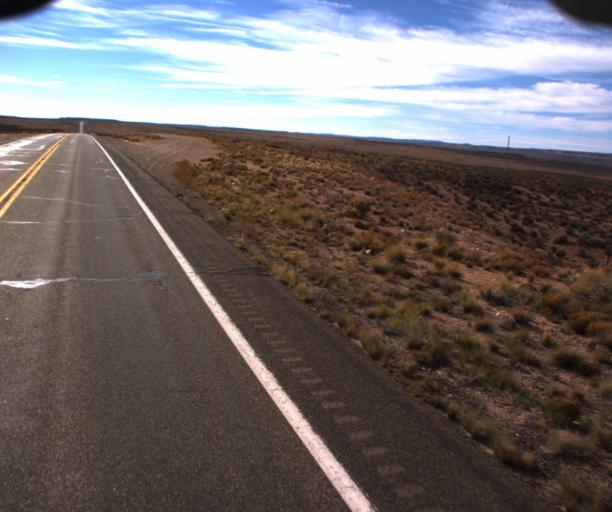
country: US
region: Arizona
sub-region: Coconino County
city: LeChee
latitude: 36.7986
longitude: -111.3015
